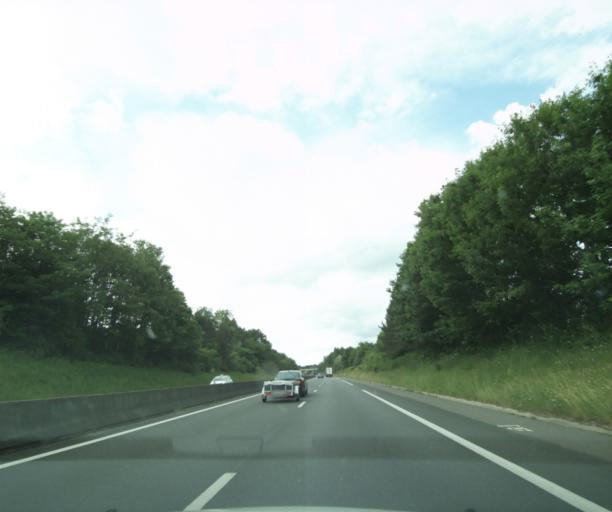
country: FR
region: Centre
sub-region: Departement du Cher
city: Vierzon
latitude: 47.2185
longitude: 2.1118
